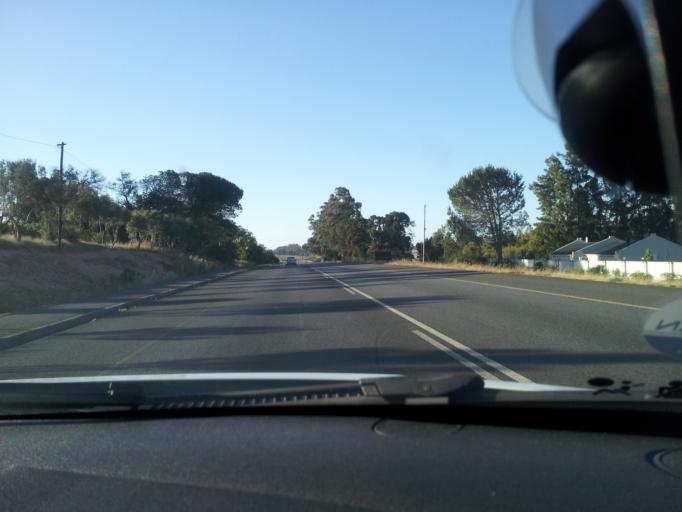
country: ZA
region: Western Cape
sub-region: Cape Winelands District Municipality
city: Stellenbosch
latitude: -33.9074
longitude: 18.8454
